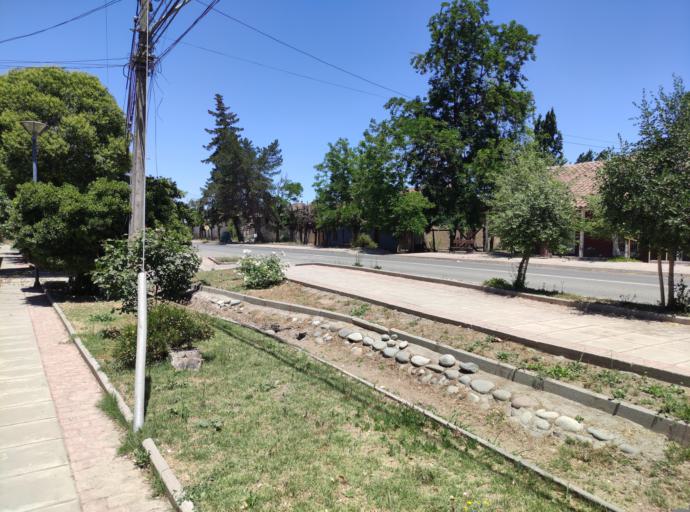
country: CL
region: O'Higgins
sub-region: Provincia de Cachapoal
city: Rancagua
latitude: -34.2236
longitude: -70.8045
